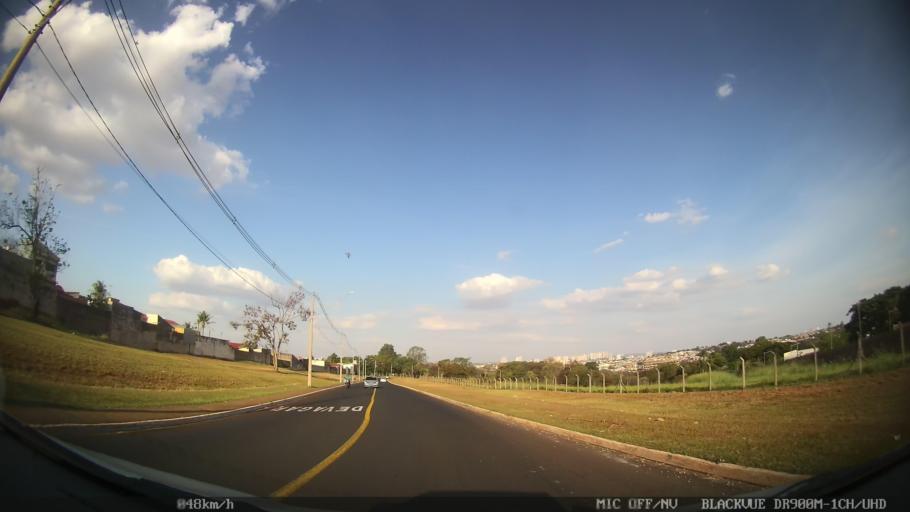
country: BR
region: Sao Paulo
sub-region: Ribeirao Preto
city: Ribeirao Preto
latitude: -21.1689
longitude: -47.8463
